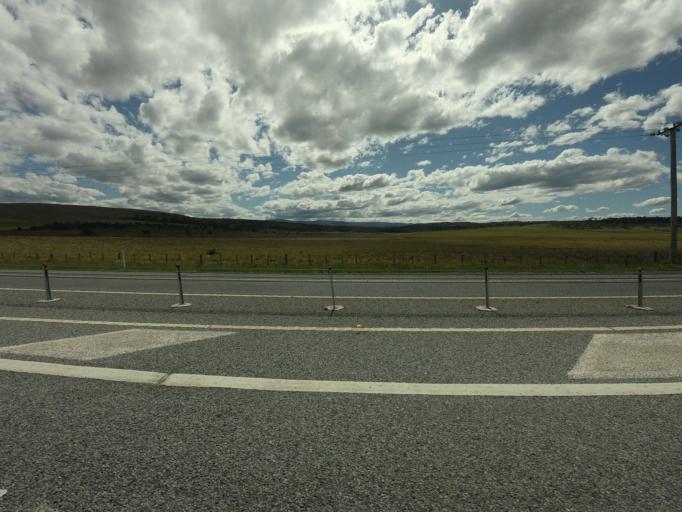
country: AU
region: Tasmania
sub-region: Northern Midlands
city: Evandale
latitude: -42.0991
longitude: 147.4527
